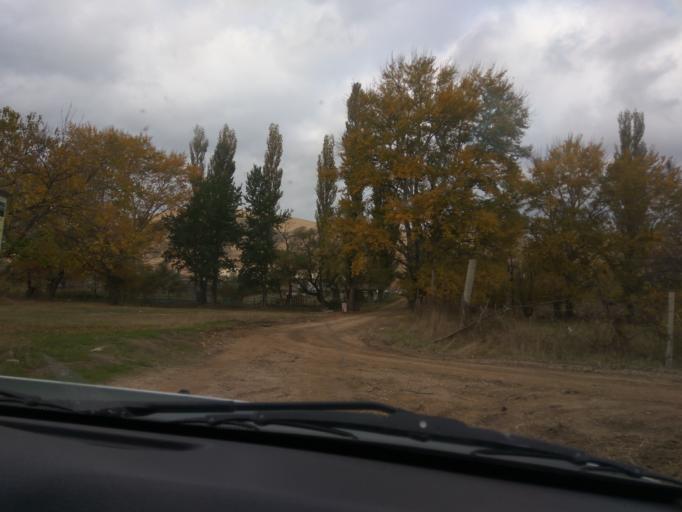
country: RU
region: Dagestan
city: Korkmaskala
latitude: 43.0019
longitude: 47.2391
